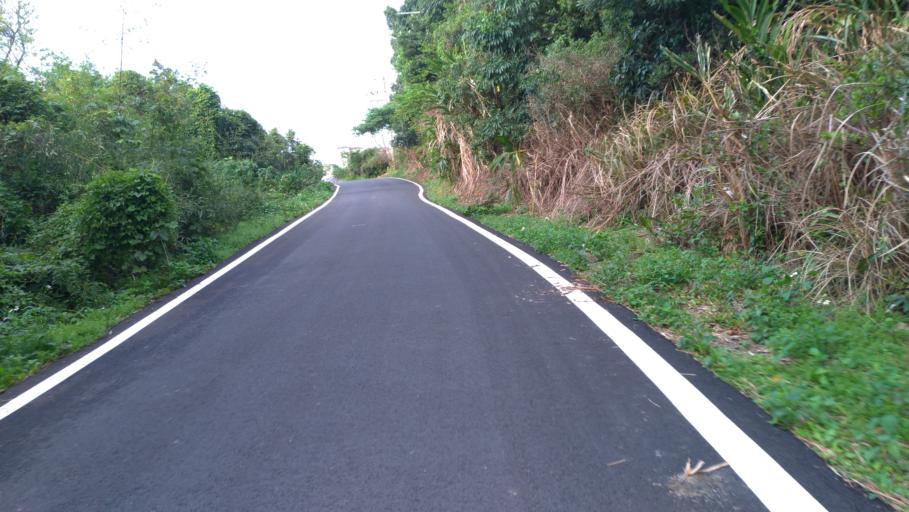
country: TW
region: Taiwan
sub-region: Hsinchu
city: Hsinchu
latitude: 24.7525
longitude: 120.9905
